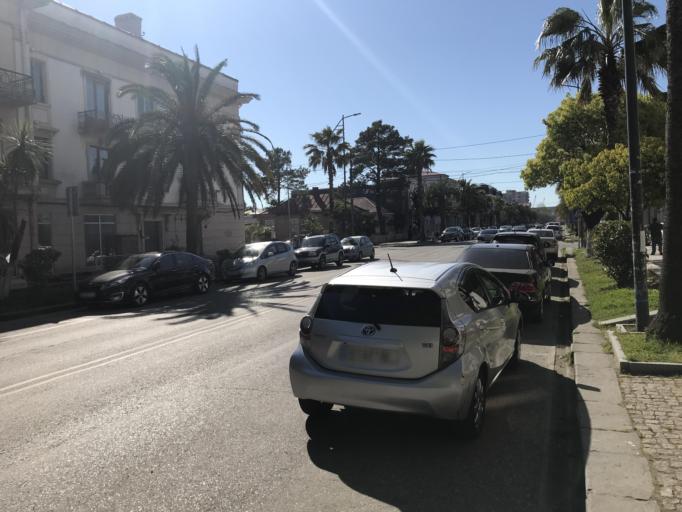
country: GE
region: Samegrelo and Zemo Svaneti
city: P'ot'i
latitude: 42.1453
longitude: 41.6686
